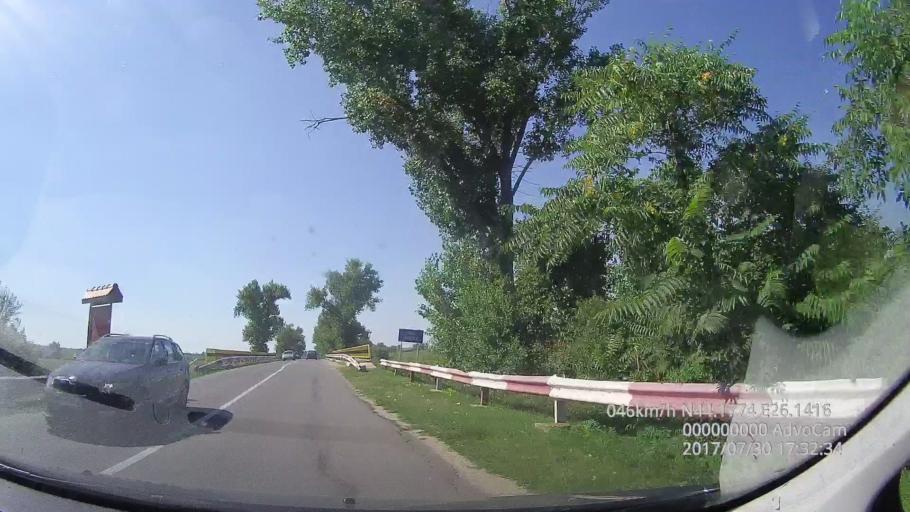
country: RO
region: Giurgiu
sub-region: Comuna Comana
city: Comana
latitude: 44.1777
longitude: 26.1412
